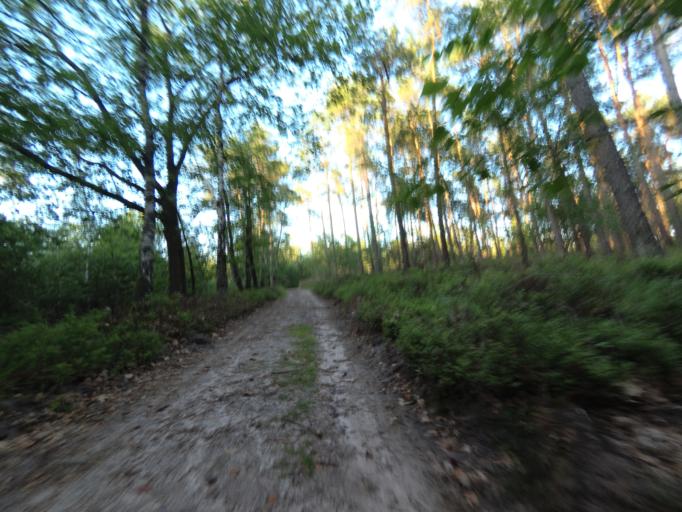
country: NL
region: Gelderland
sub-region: Gemeente Apeldoorn
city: Beekbergen
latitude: 52.1470
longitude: 5.8885
